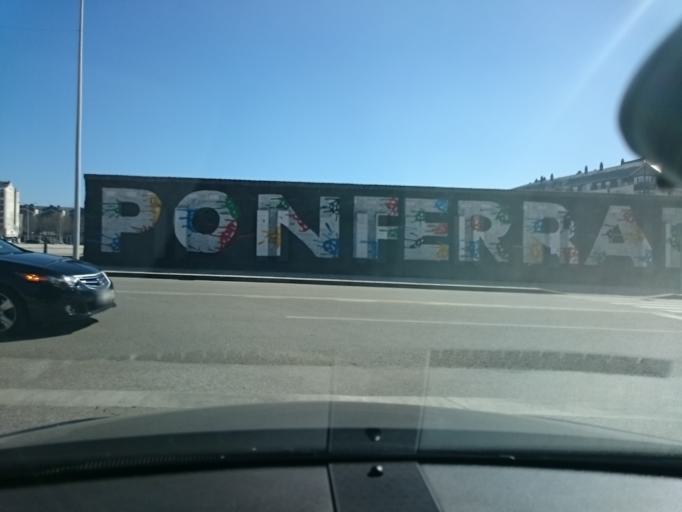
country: ES
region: Castille and Leon
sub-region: Provincia de Leon
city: Ponferrada
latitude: 42.5527
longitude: -6.6045
